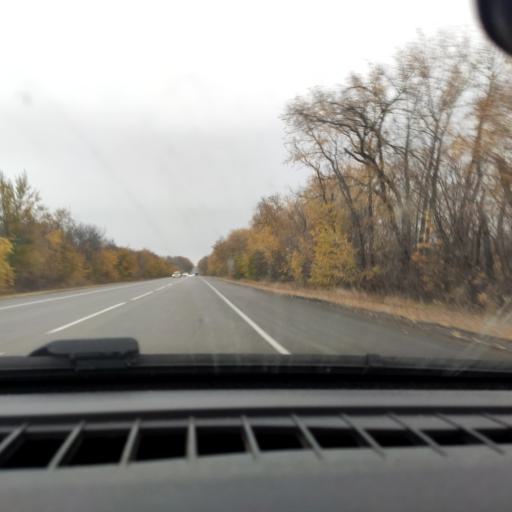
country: RU
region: Voronezj
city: Uryv-Pokrovka
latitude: 51.1516
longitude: 39.0623
